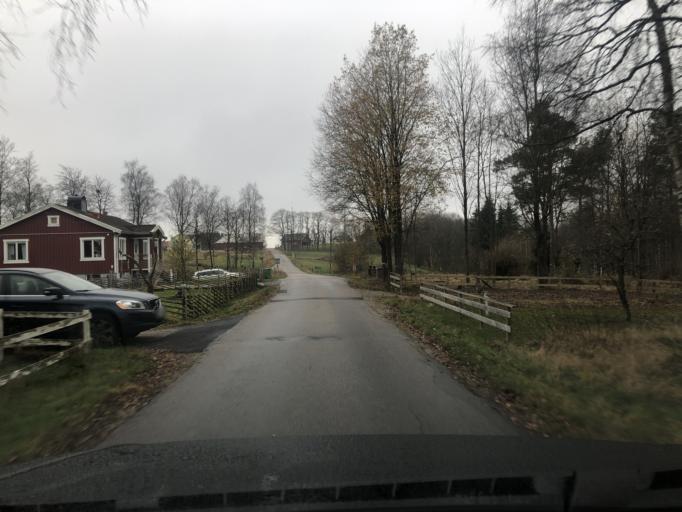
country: SE
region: Vaestra Goetaland
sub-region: Boras Kommun
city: Sjomarken
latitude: 57.7630
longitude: 12.8458
